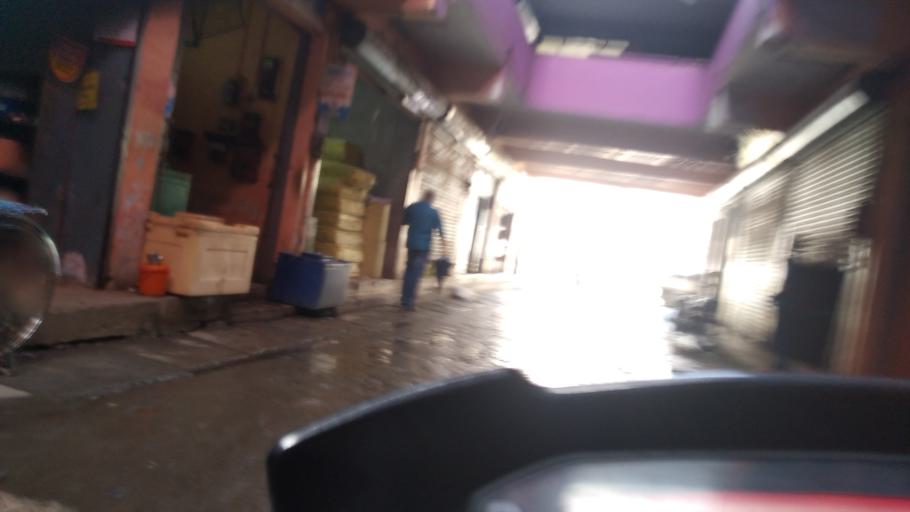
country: IN
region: Kerala
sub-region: Ernakulam
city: Cochin
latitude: 9.9790
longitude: 76.2801
